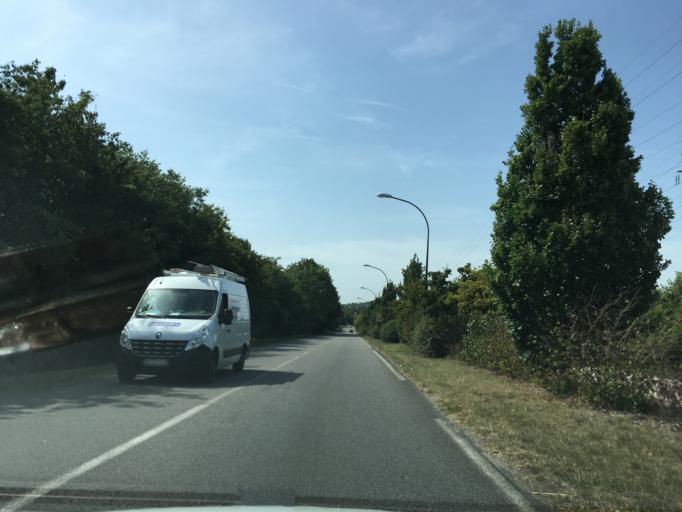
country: FR
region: Midi-Pyrenees
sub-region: Departement du Tarn
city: Castres
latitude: 43.6212
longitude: 2.2654
